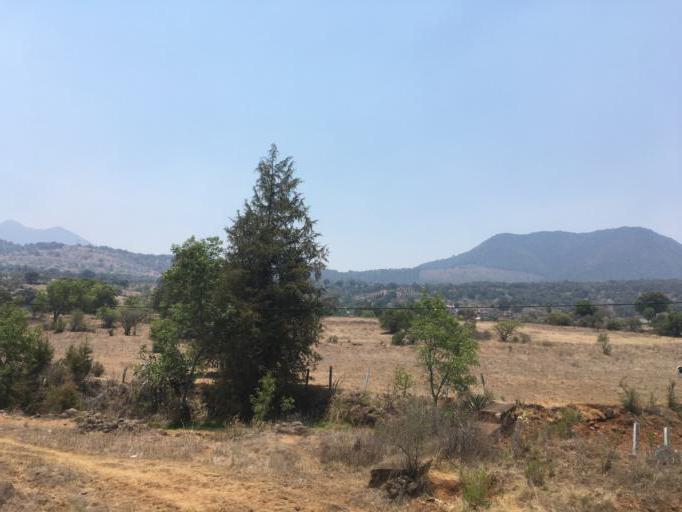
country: MX
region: Michoacan
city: Quiroga
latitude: 19.6557
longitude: -101.4981
